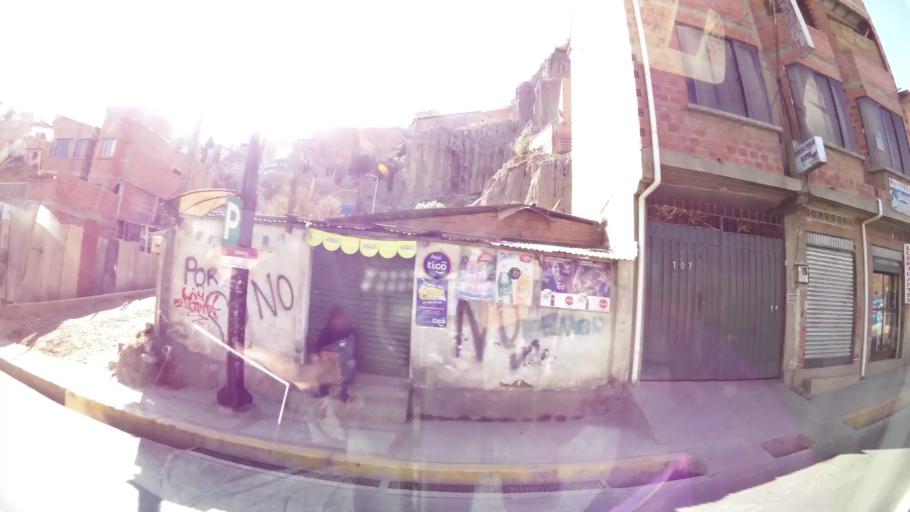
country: BO
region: La Paz
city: La Paz
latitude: -16.5197
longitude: -68.1252
